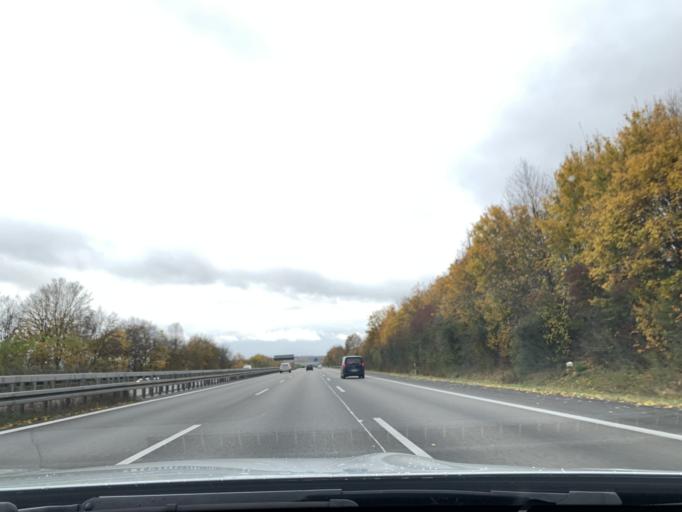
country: DE
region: Baden-Wuerttemberg
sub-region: Regierungsbezirk Stuttgart
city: Abstatt
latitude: 49.0777
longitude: 9.2853
